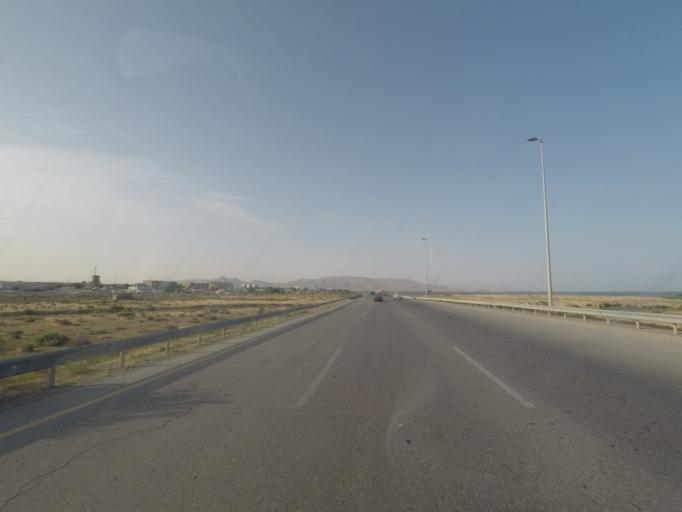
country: AZ
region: Baki
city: Qobustan
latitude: 40.1601
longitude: 49.4635
